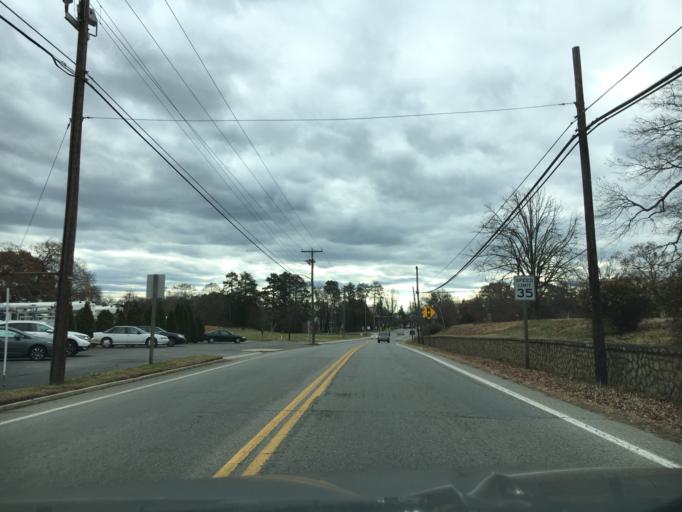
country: US
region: Virginia
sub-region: Halifax County
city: South Boston
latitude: 36.7206
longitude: -78.9037
